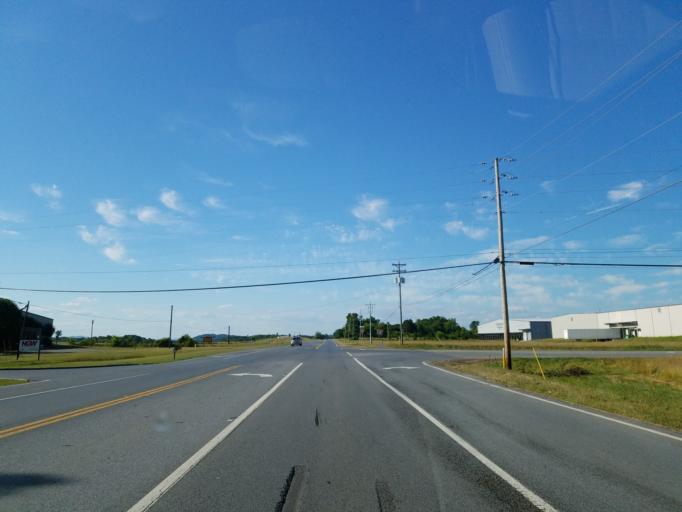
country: US
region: Georgia
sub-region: Gordon County
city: Calhoun
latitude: 34.4428
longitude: -84.9358
